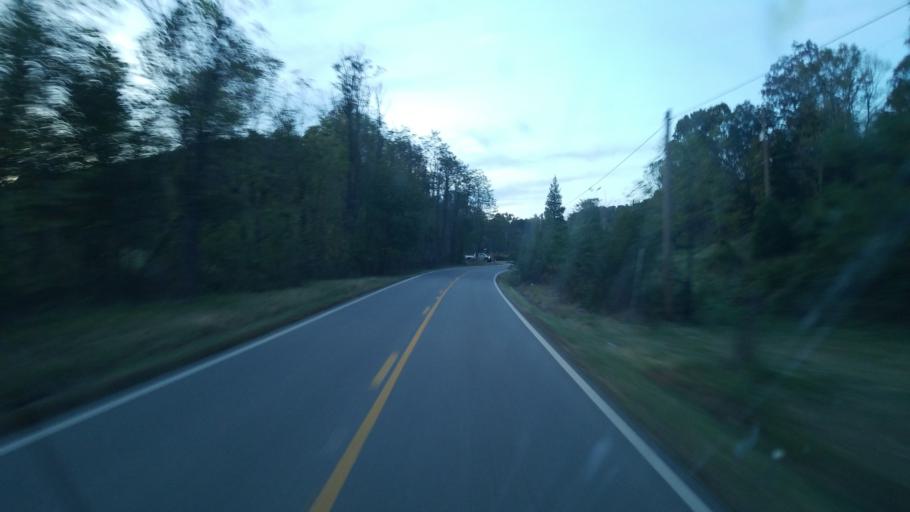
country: US
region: Ohio
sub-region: Meigs County
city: Pomeroy
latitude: 39.0861
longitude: -82.0924
